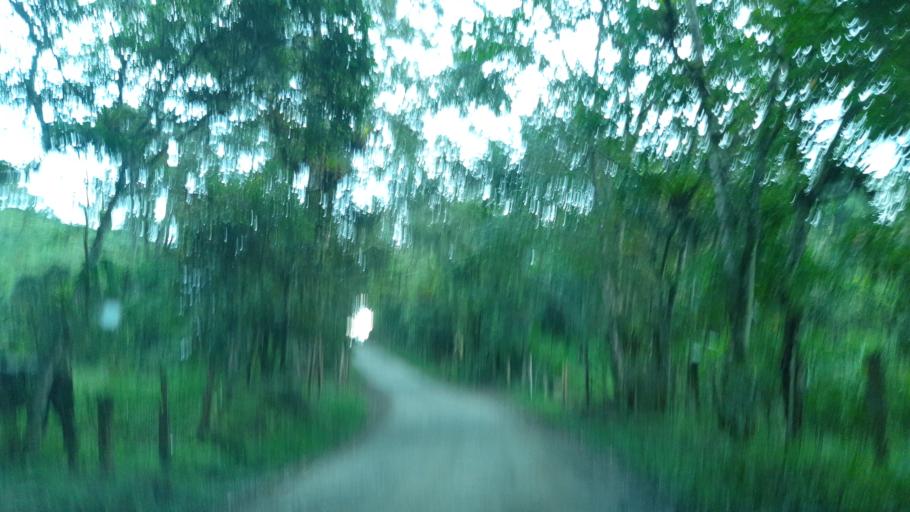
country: CO
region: Boyaca
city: Garagoa
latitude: 5.1078
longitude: -73.3564
